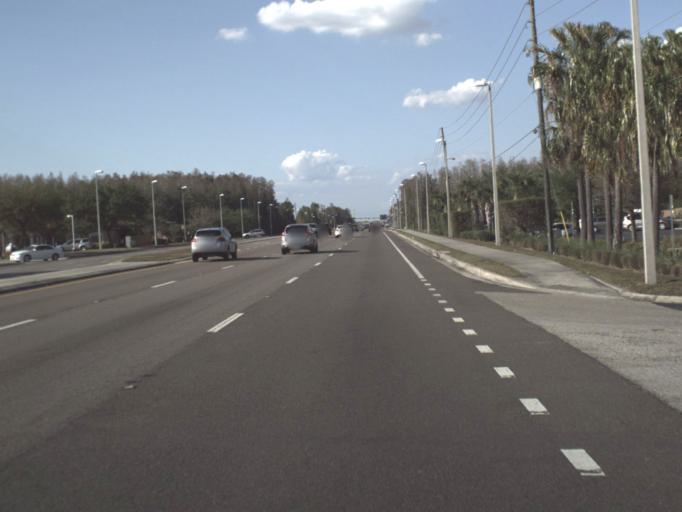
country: US
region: Florida
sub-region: Orange County
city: Hunters Creek
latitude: 28.3558
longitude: -81.4044
